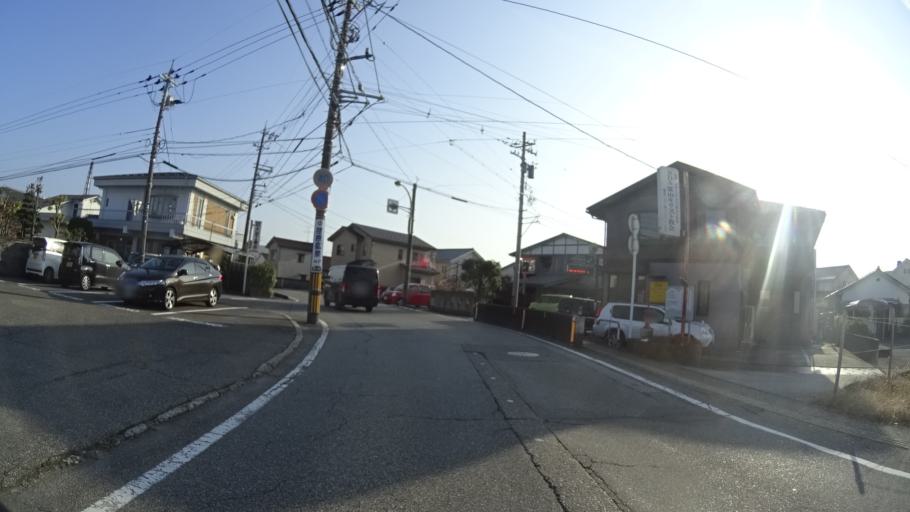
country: JP
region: Toyama
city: Toyama-shi
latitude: 36.6975
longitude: 137.2649
